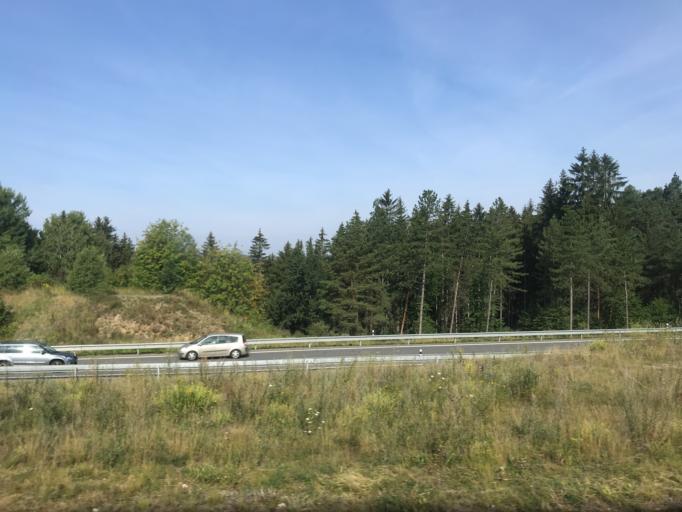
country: CZ
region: Jihocesky
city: Chotoviny
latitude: 49.5017
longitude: 14.6556
